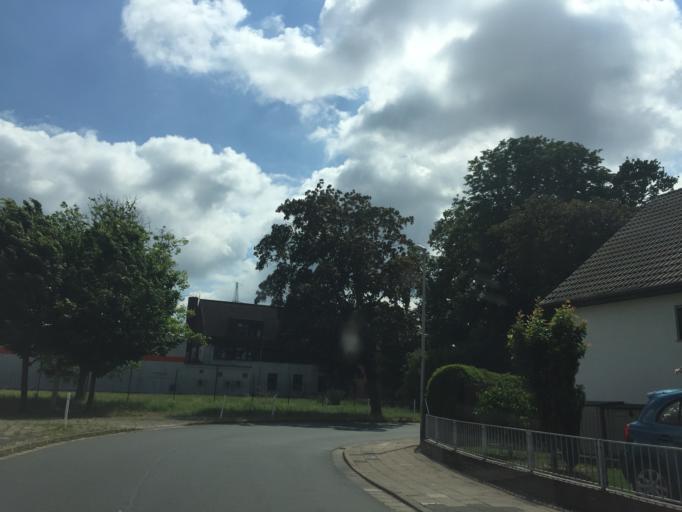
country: DE
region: Lower Saxony
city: Hildesheim
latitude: 52.1723
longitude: 9.9910
